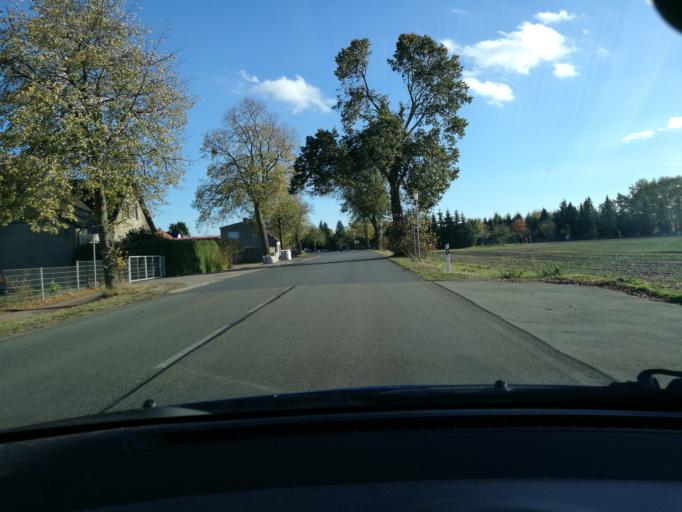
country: DE
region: Brandenburg
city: Karstadt
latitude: 53.1375
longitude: 11.7782
